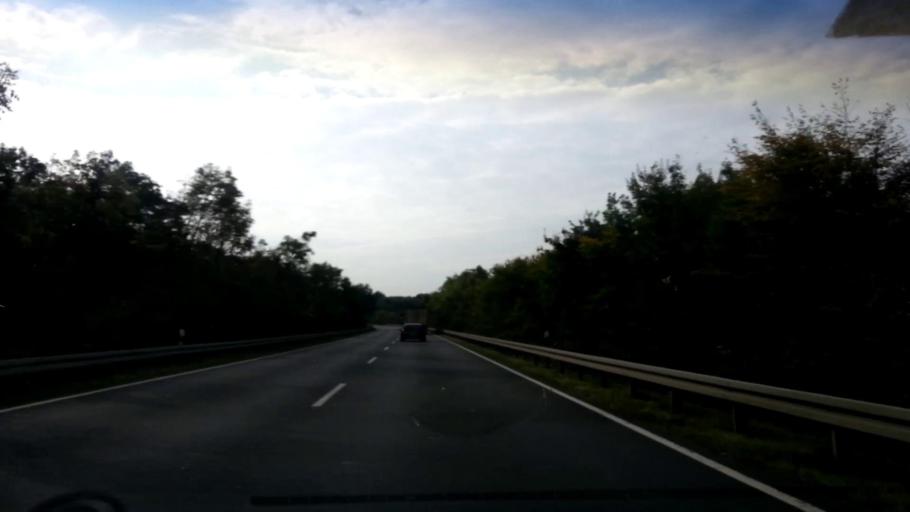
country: DE
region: Bavaria
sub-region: Regierungsbezirk Unterfranken
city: Prichsenstadt
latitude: 49.8352
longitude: 10.3536
